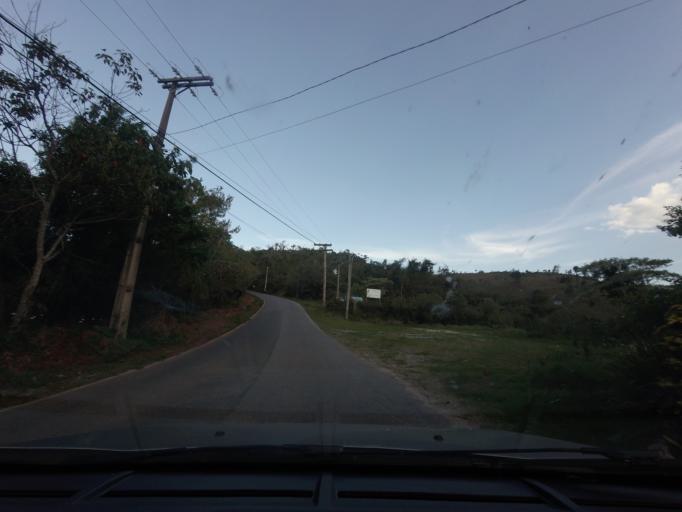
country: BR
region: Sao Paulo
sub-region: Campos Do Jordao
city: Campos do Jordao
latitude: -22.7477
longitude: -45.5643
